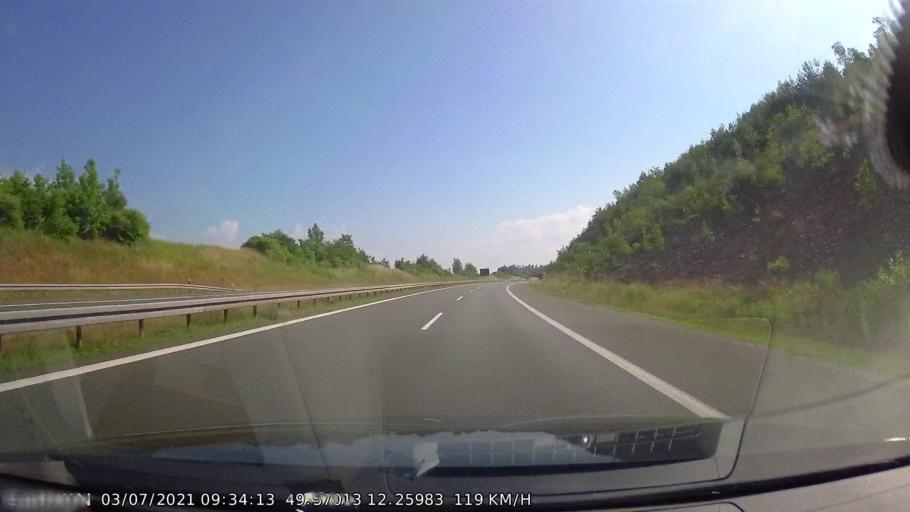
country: DE
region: Bavaria
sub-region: Upper Palatinate
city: Leuchtenberg
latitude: 49.5703
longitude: 12.2599
